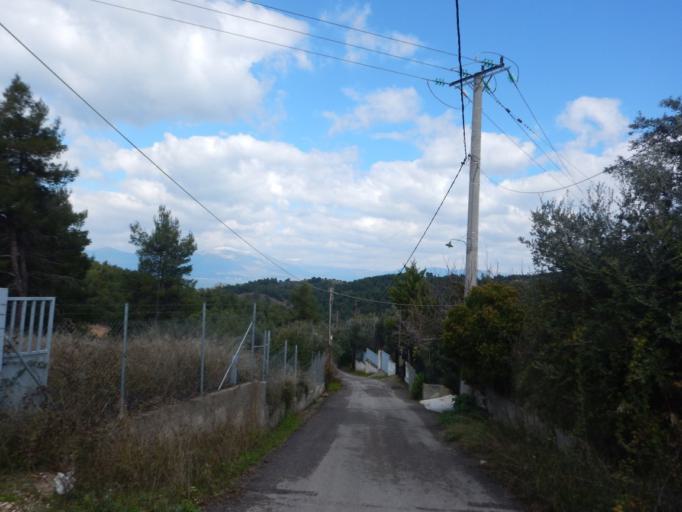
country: GR
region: Attica
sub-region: Nomarchia Anatolikis Attikis
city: Markopoulo Oropou
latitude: 38.2953
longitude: 23.8249
